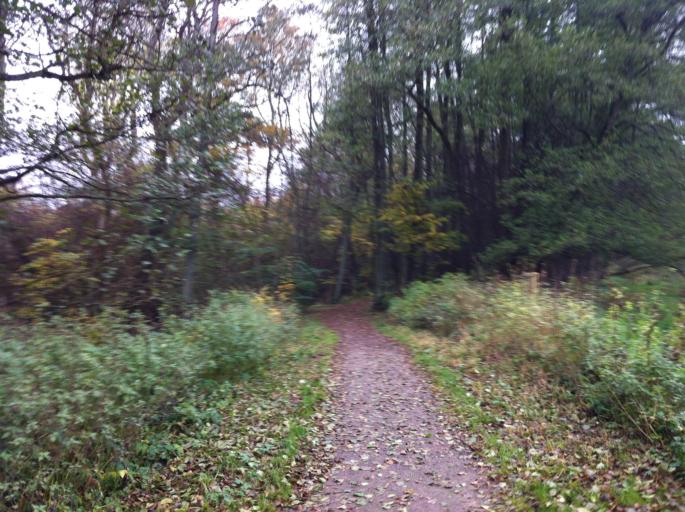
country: SE
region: Skane
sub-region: Helsingborg
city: Gantofta
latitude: 55.9937
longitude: 12.8049
